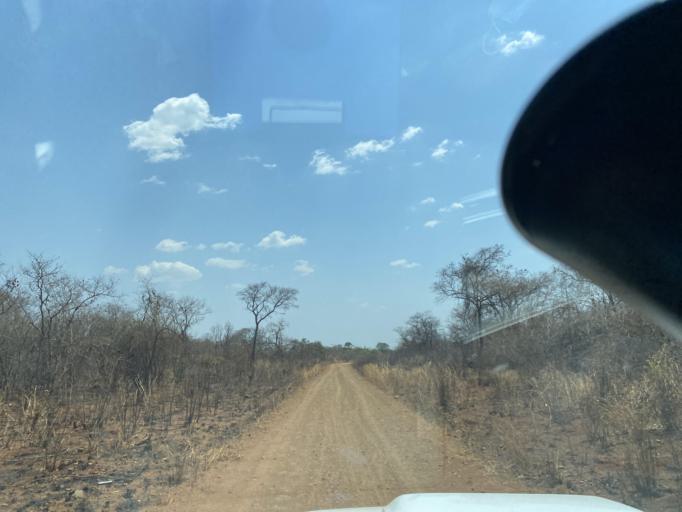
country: ZM
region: Lusaka
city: Lusaka
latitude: -15.5091
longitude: 27.9927
